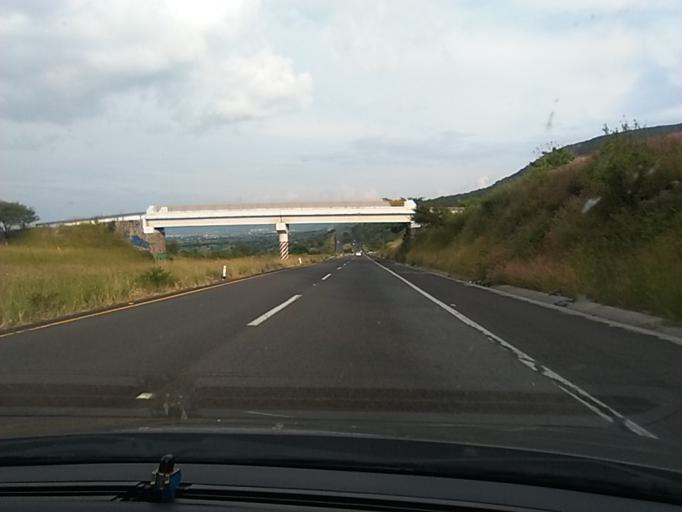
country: MX
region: Michoacan
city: Copandaro de Galeana
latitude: 19.9009
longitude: -101.2652
